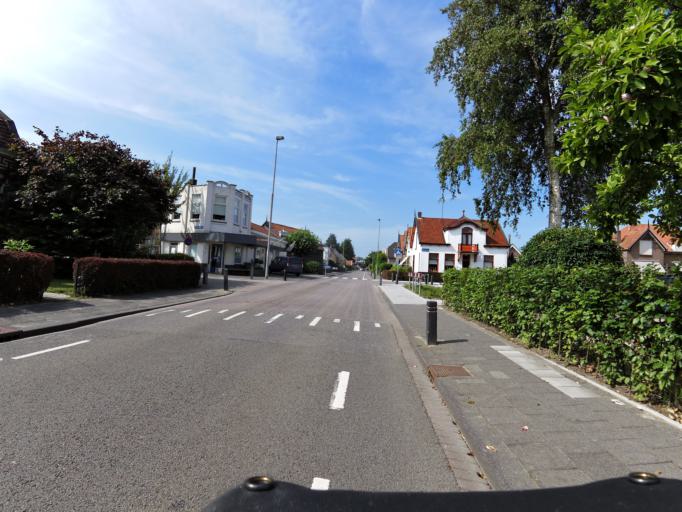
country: NL
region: South Holland
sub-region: Gemeente Goeree-Overflakkee
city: Middelharnis
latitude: 51.7585
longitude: 4.1558
